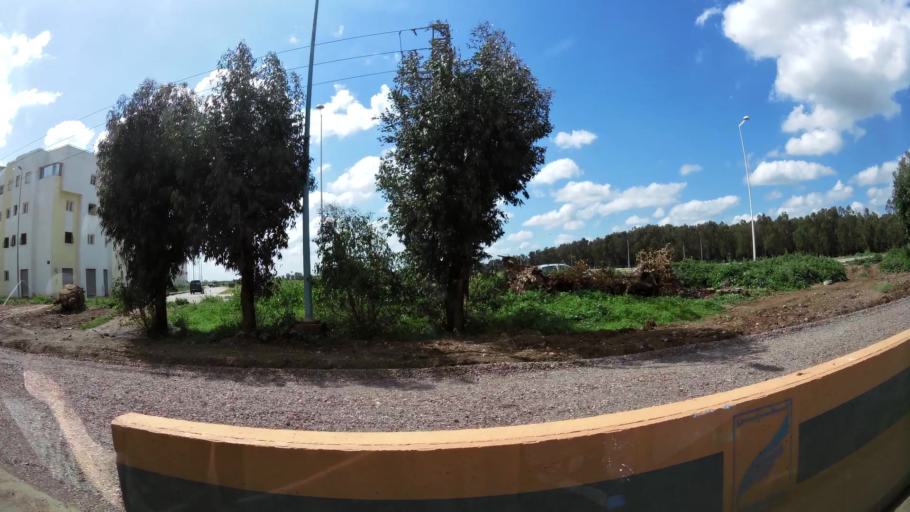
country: MA
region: Chaouia-Ouardigha
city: Nouaseur
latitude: 33.3670
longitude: -7.5440
